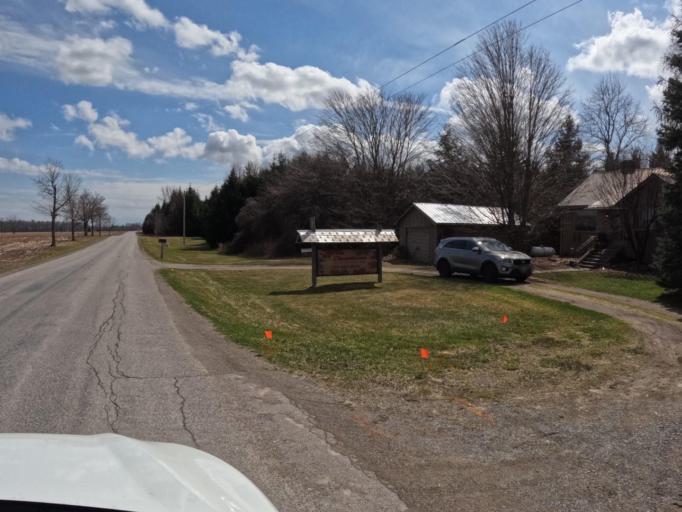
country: CA
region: Ontario
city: Norfolk County
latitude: 42.9056
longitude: -80.1917
